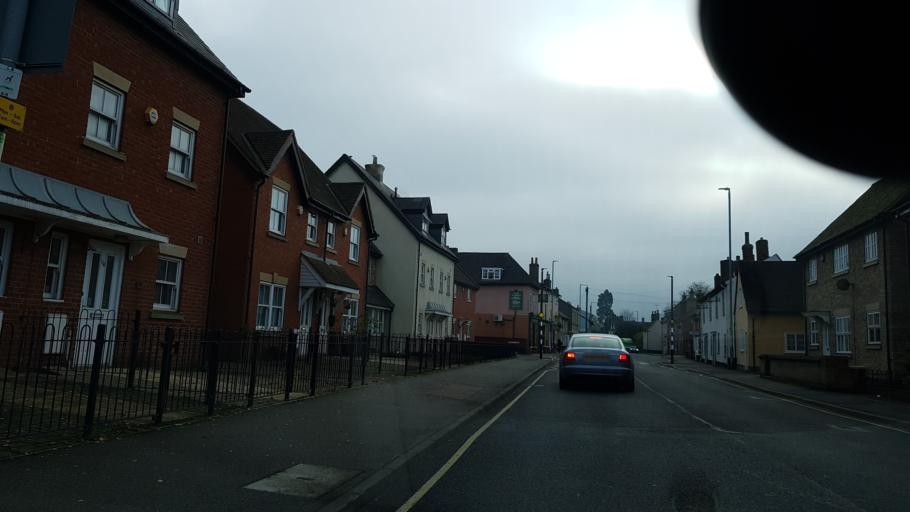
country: GB
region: England
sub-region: Central Bedfordshire
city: Biggleswade
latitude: 52.0908
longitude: -0.2676
